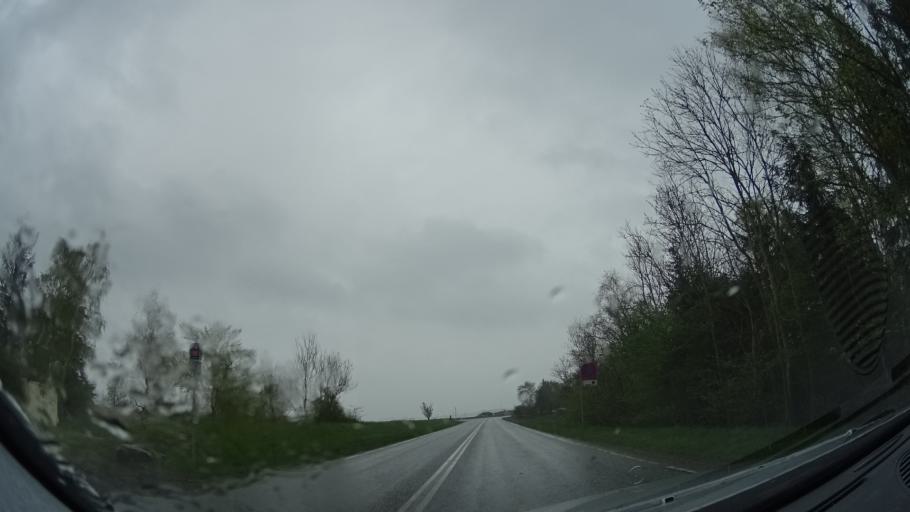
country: DK
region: Zealand
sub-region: Odsherred Kommune
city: Asnaes
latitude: 55.7798
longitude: 11.6074
